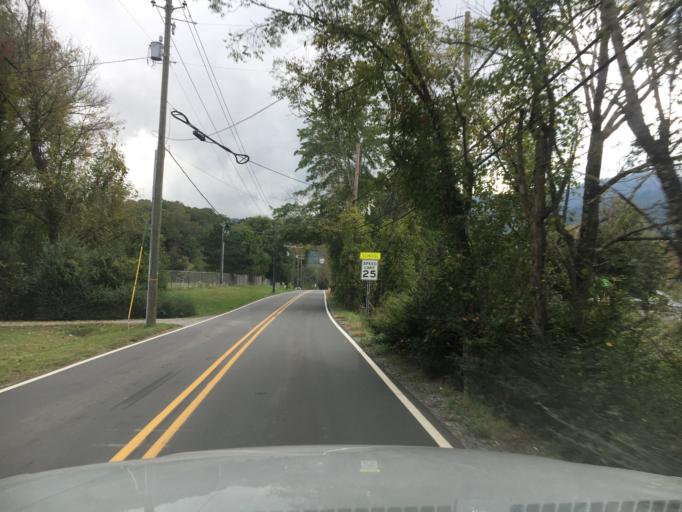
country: US
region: North Carolina
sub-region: Buncombe County
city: Swannanoa
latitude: 35.6041
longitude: -82.4048
